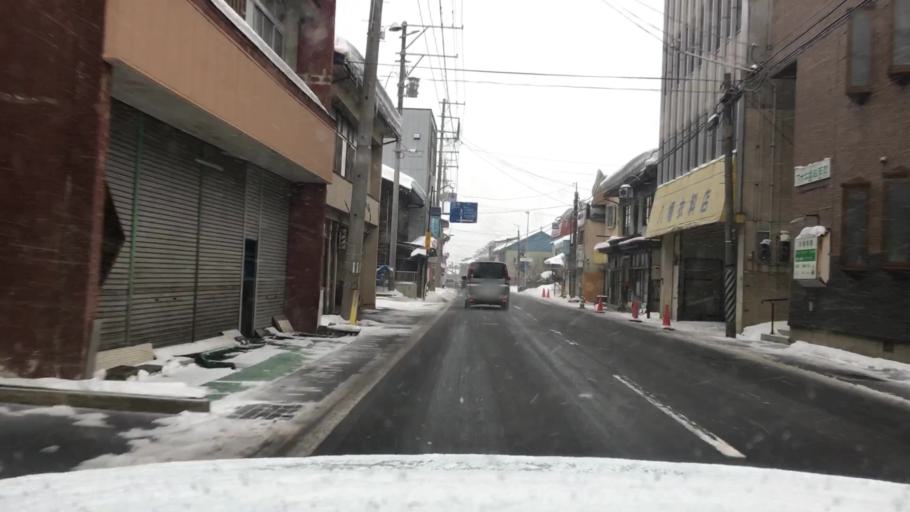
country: JP
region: Iwate
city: Ichinohe
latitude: 40.0992
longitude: 141.0479
